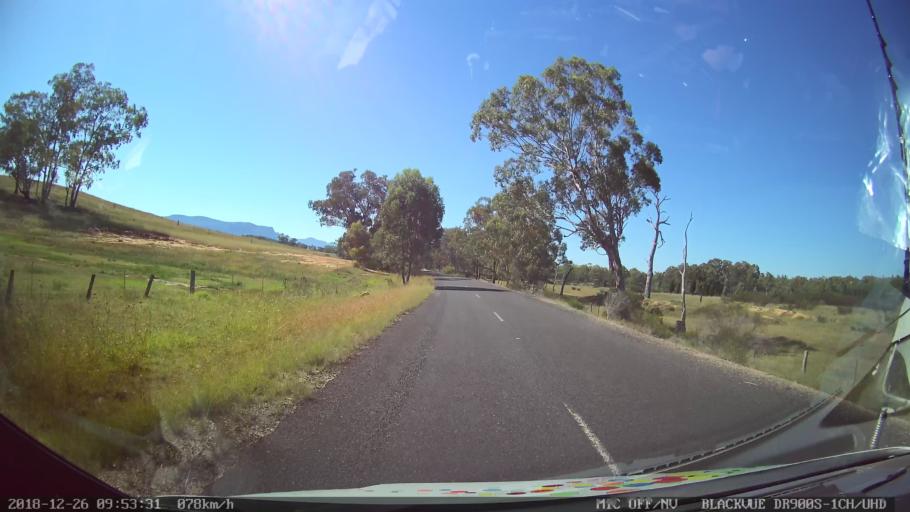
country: AU
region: New South Wales
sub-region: Mid-Western Regional
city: Kandos
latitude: -33.0217
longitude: 150.1537
